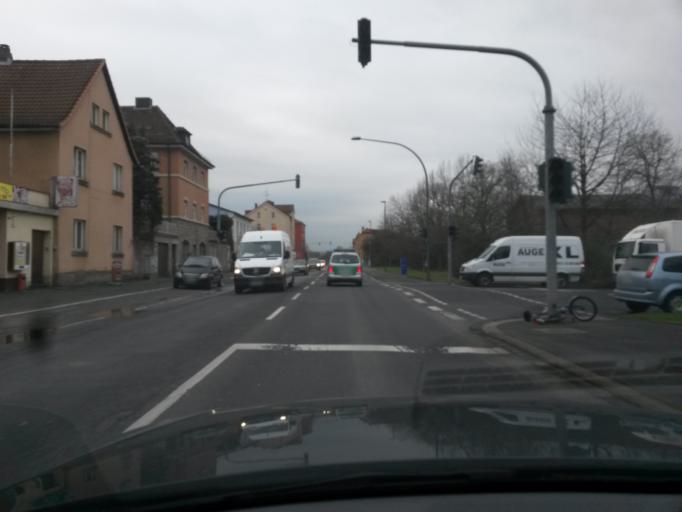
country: DE
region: Bavaria
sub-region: Regierungsbezirk Unterfranken
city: Wuerzburg
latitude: 49.7965
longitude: 9.9634
